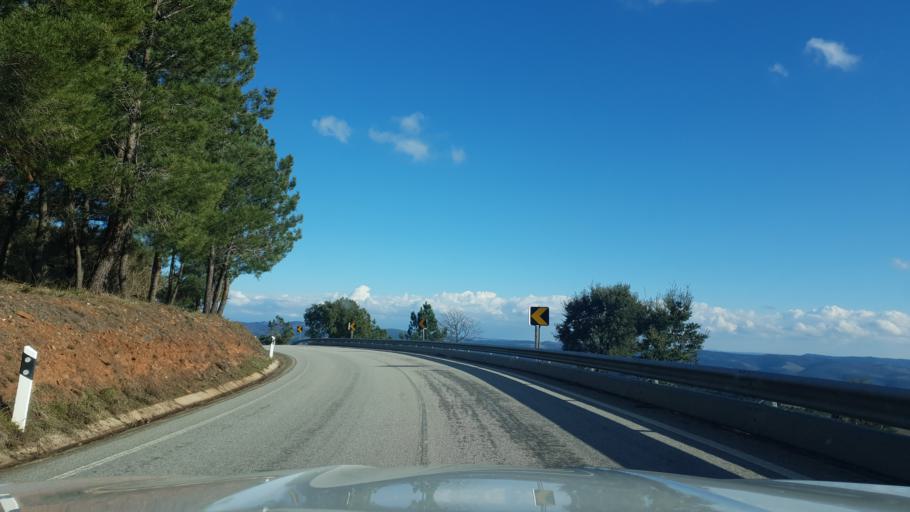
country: PT
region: Braganca
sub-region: Torre de Moncorvo
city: Torre de Moncorvo
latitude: 41.1790
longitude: -6.9284
